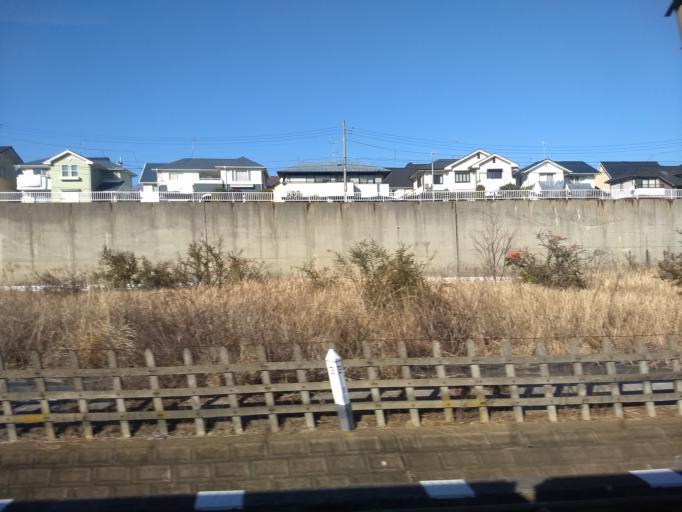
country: JP
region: Chiba
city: Shiroi
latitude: 35.7843
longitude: 140.0273
